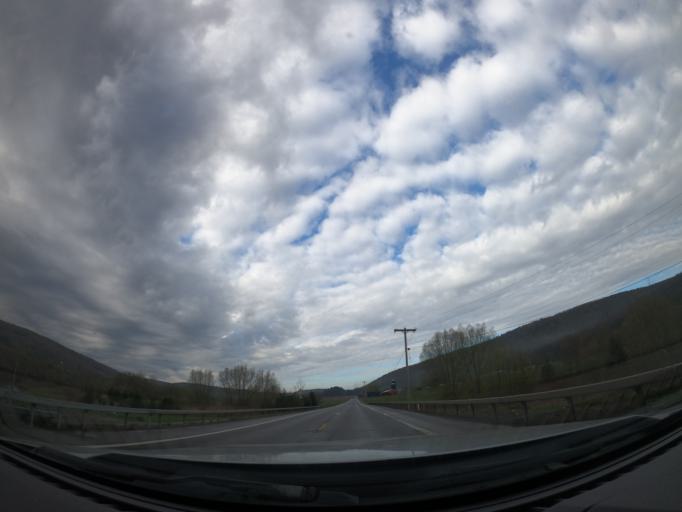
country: US
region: New York
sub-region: Cortland County
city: McGraw
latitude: 42.7244
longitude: -75.9708
